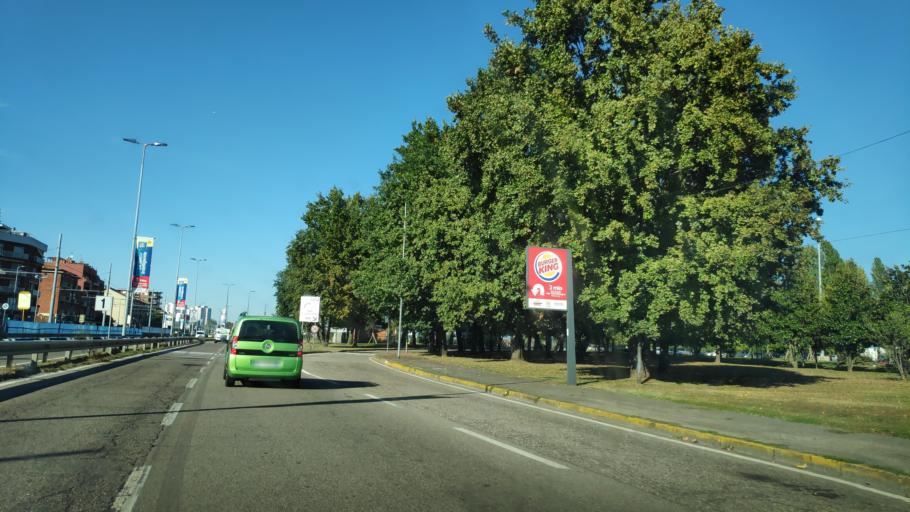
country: IT
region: Lombardy
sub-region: Citta metropolitana di Milano
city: Rozzano
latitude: 45.3932
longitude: 9.1731
